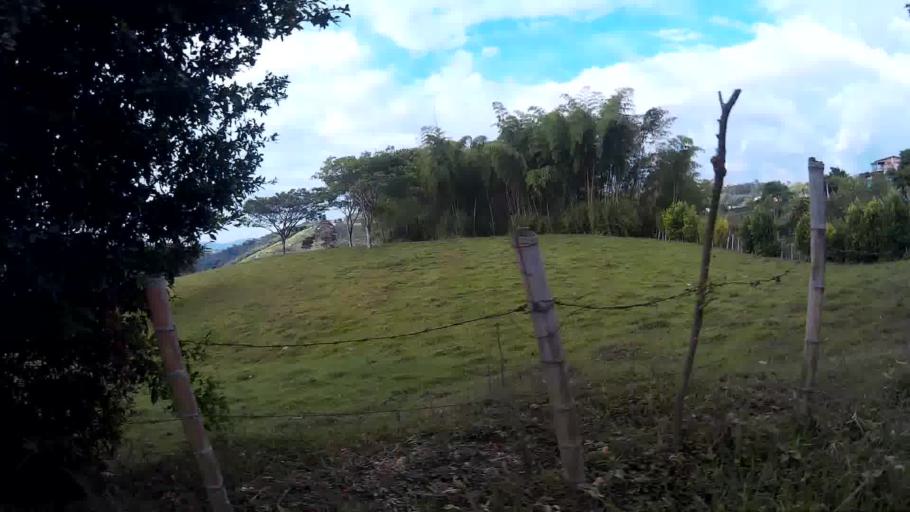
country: CO
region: Valle del Cauca
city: Ulloa
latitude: 4.7313
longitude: -75.7260
